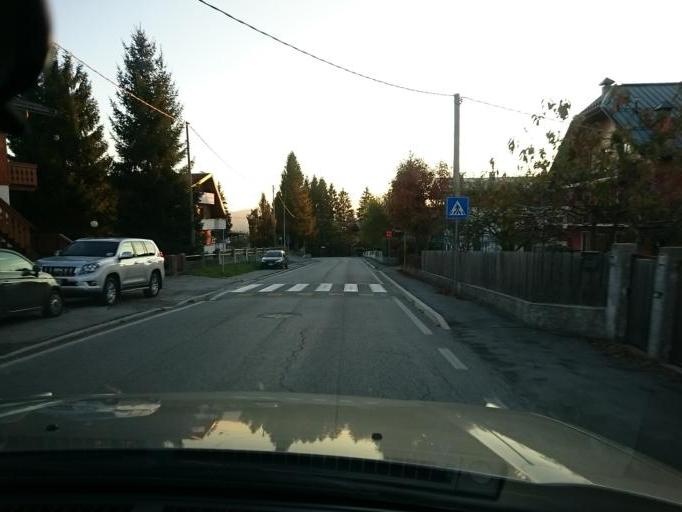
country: IT
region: Veneto
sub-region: Provincia di Vicenza
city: Canove di Roana
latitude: 45.8729
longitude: 11.4812
